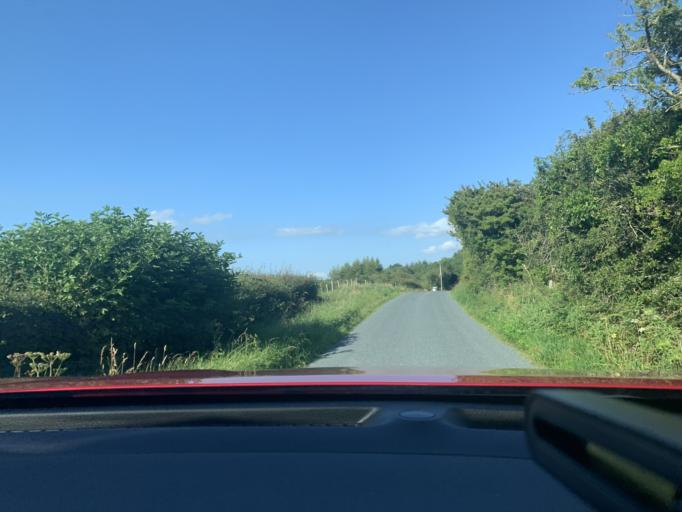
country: IE
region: Connaught
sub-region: Sligo
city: Tobercurry
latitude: 54.1546
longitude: -8.6599
